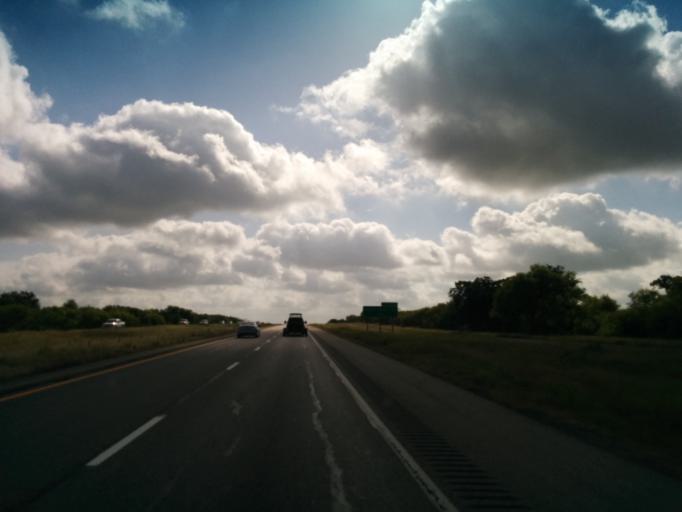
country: US
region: Texas
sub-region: Caldwell County
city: Luling
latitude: 29.6391
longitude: -97.7186
